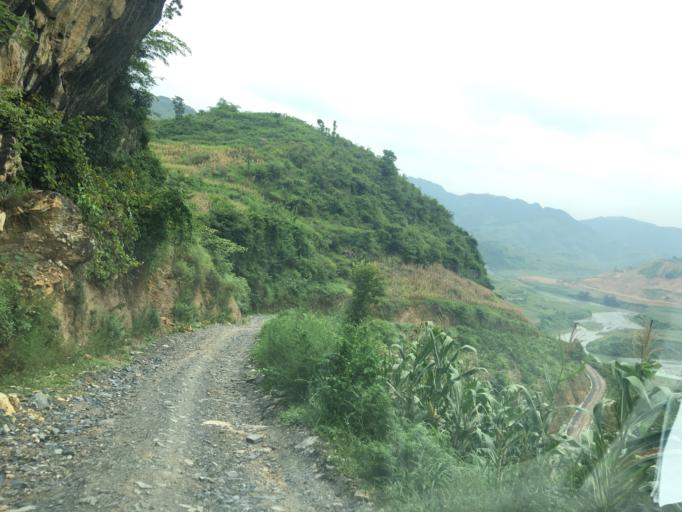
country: CN
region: Guangxi Zhuangzu Zizhiqu
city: Xinzhou
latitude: 25.1764
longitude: 105.7311
